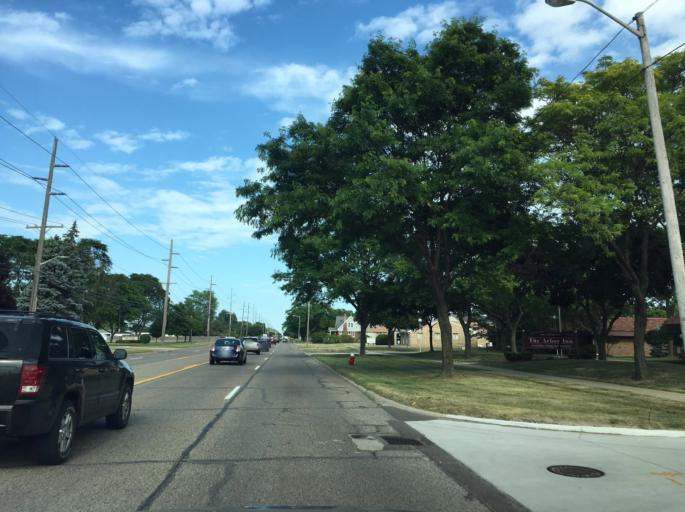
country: US
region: Michigan
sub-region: Macomb County
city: Fraser
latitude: 42.5380
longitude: -82.9840
